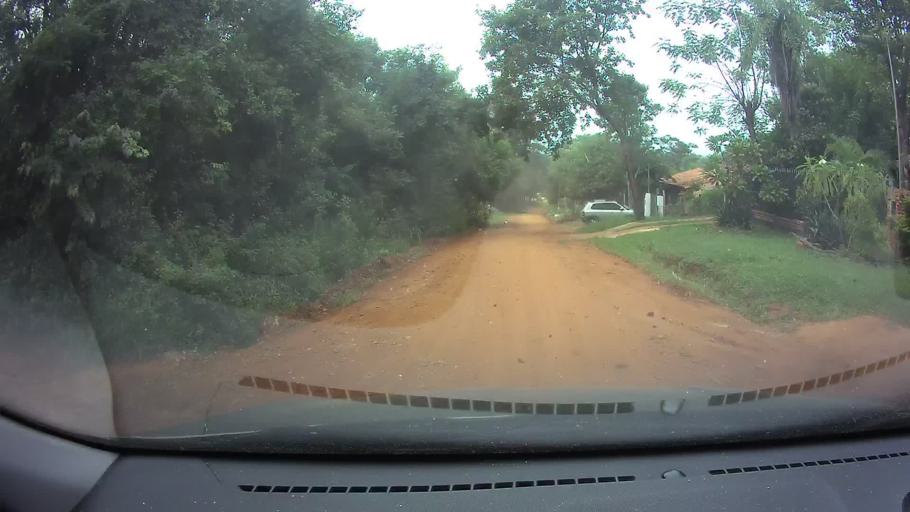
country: PY
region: Central
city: Limpio
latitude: -25.2378
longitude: -57.4570
